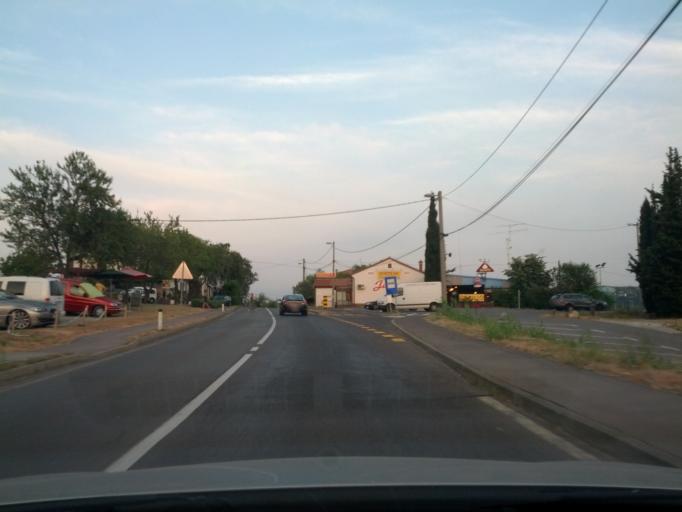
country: SI
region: Izola-Isola
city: Jagodje
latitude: 45.5294
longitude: 13.6371
